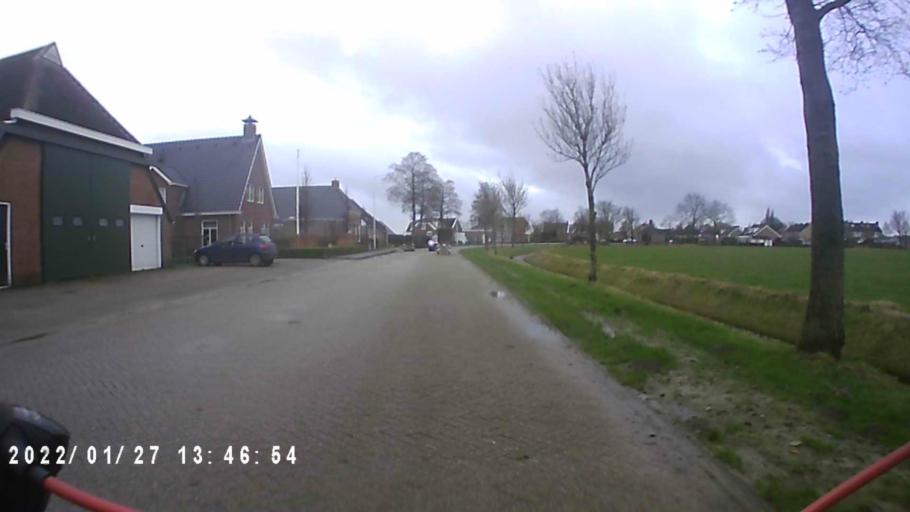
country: NL
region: Friesland
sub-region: Gemeente Kollumerland en Nieuwkruisland
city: Kollum
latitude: 53.3026
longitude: 6.1949
